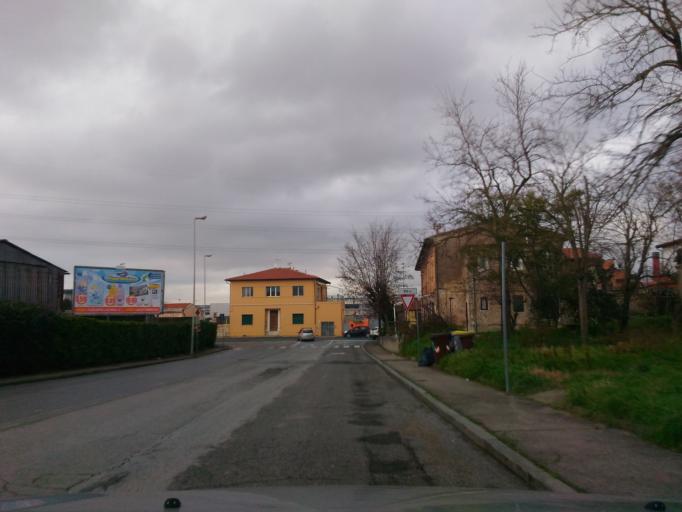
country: IT
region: Tuscany
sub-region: Provincia di Livorno
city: Livorno
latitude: 43.5733
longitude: 10.3367
